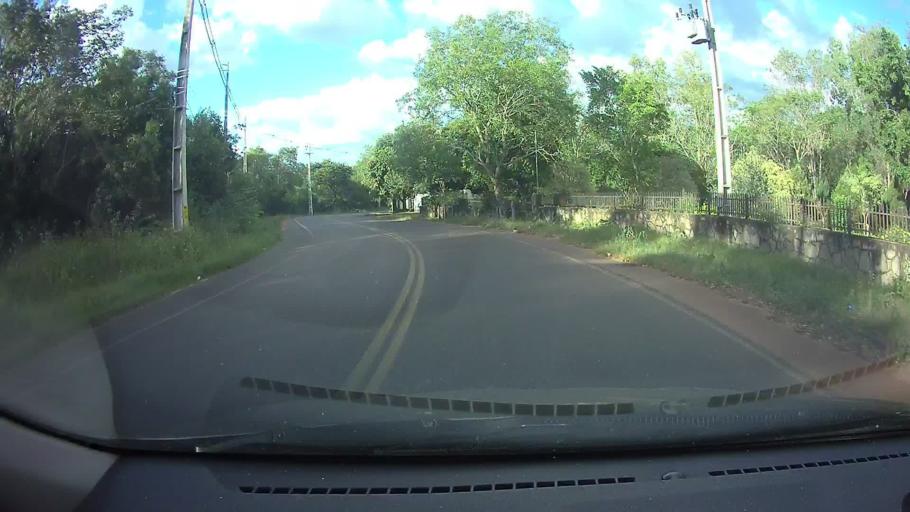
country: PY
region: Cordillera
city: Altos
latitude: -25.2477
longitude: -57.2351
